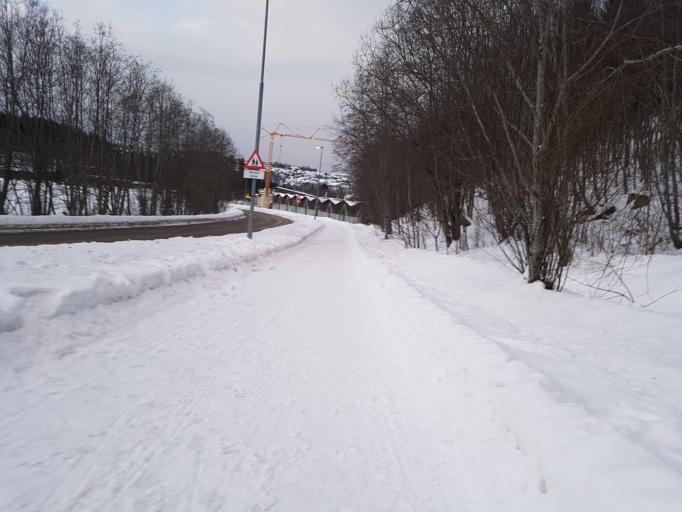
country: NO
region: Sor-Trondelag
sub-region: Trondheim
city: Trondheim
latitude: 63.3800
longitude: 10.3803
